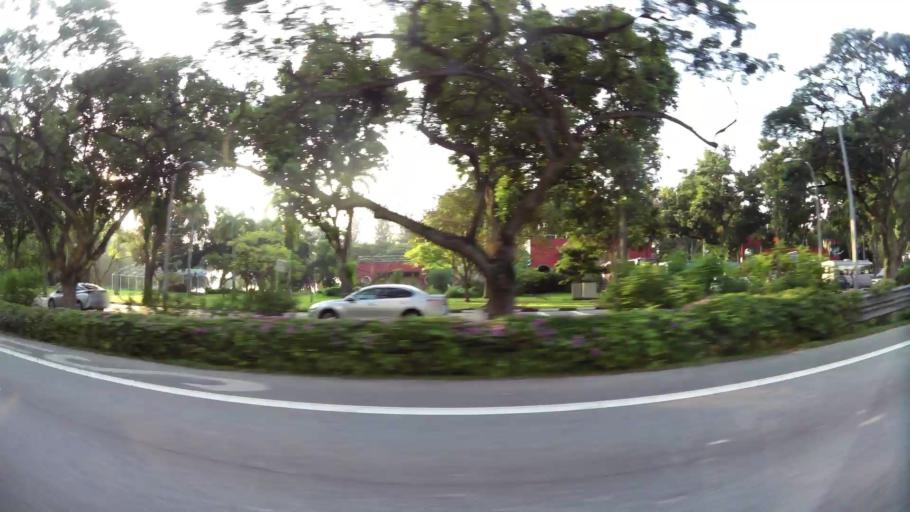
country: SG
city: Singapore
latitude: 1.2989
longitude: 103.9027
